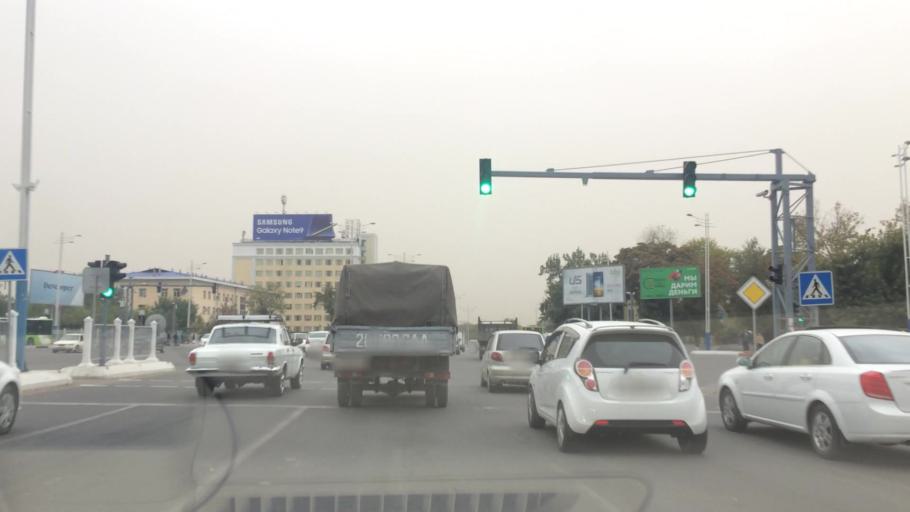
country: UZ
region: Toshkent Shahri
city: Bektemir
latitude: 41.3052
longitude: 69.3075
